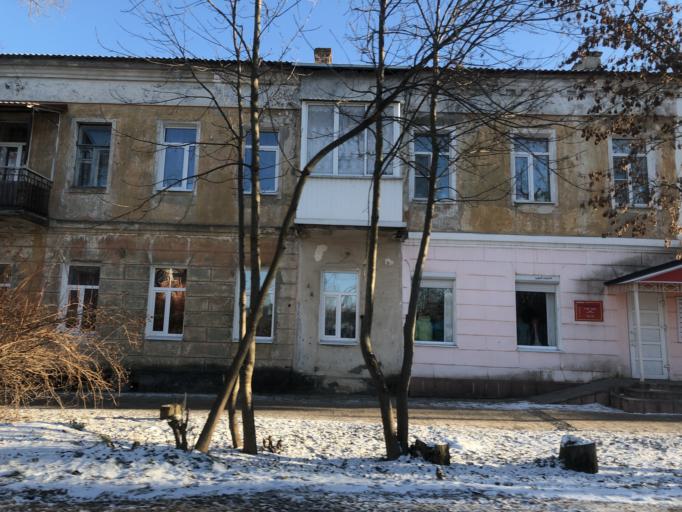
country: RU
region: Tverskaya
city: Rzhev
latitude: 56.2600
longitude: 34.3504
